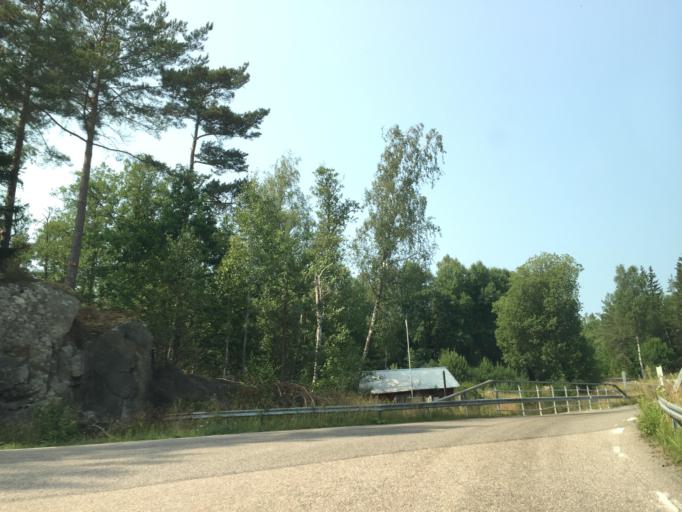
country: SE
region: Vaestra Goetaland
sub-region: Trollhattan
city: Sjuntorp
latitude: 58.3069
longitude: 12.1283
